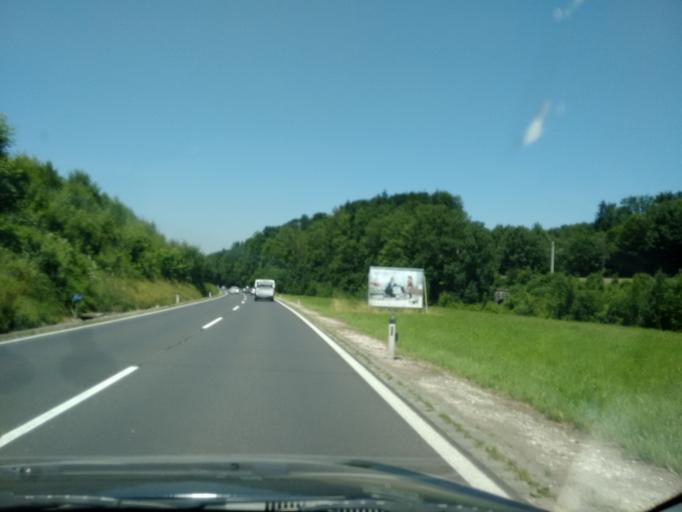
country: AT
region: Upper Austria
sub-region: Politischer Bezirk Gmunden
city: Altmunster
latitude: 47.9444
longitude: 13.7560
